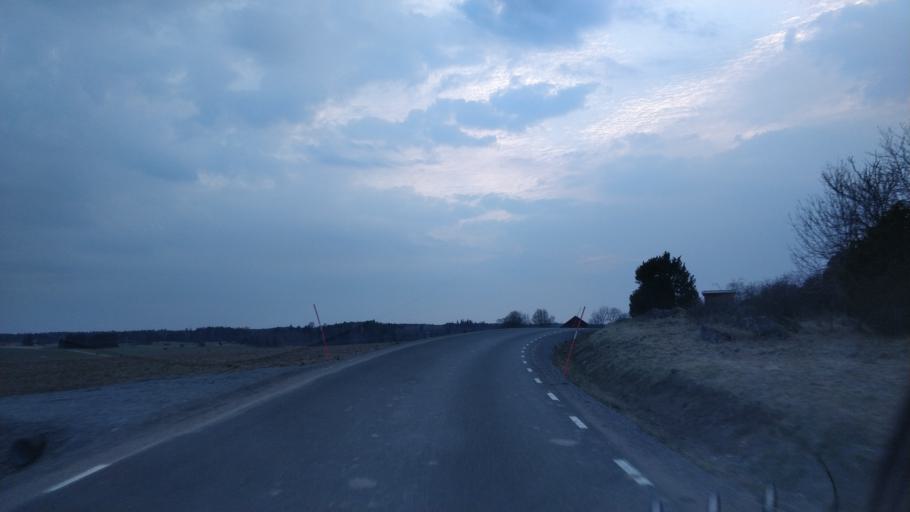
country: SE
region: Uppsala
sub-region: Enkopings Kommun
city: Orsundsbro
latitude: 59.7194
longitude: 17.2615
